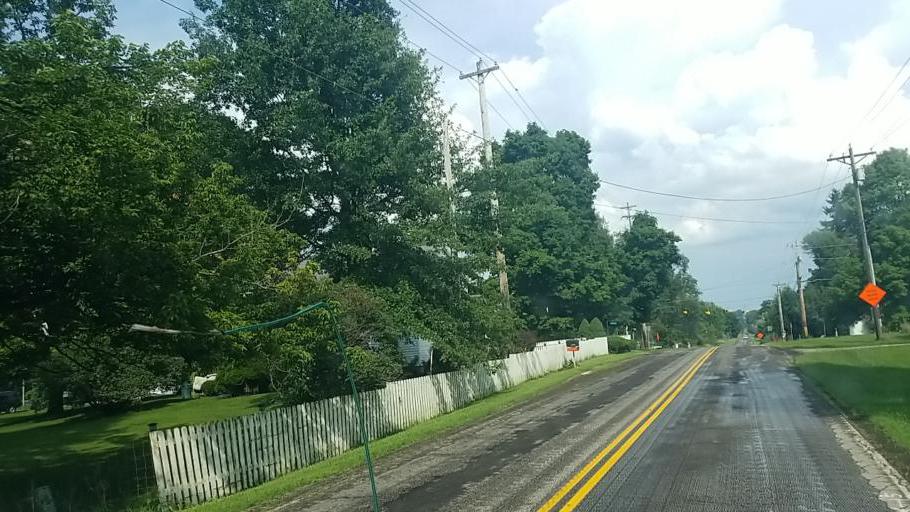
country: US
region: Ohio
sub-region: Medina County
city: Westfield Center
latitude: 41.0272
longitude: -81.9677
